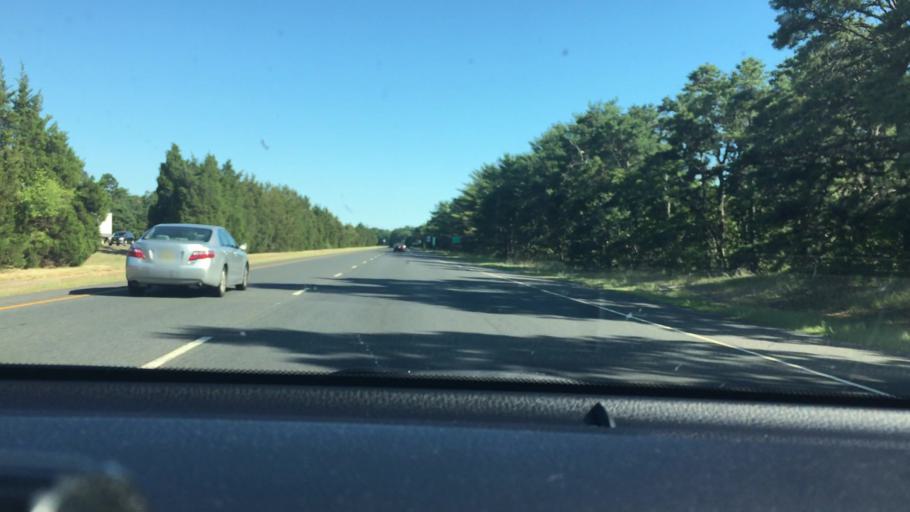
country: US
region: New Jersey
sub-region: Cumberland County
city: South Vineland
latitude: 39.4442
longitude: -75.0626
